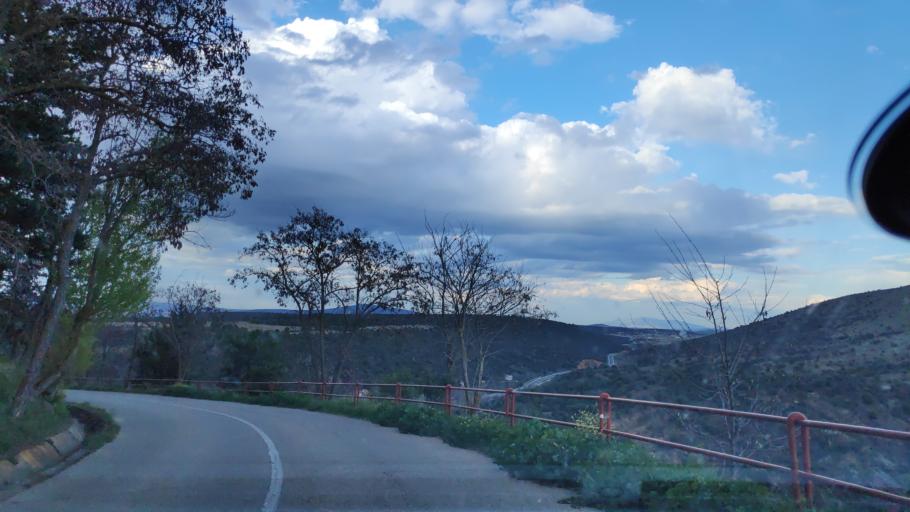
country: ES
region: Castille and Leon
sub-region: Provincia de Soria
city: Soria
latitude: 41.7602
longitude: -2.4579
